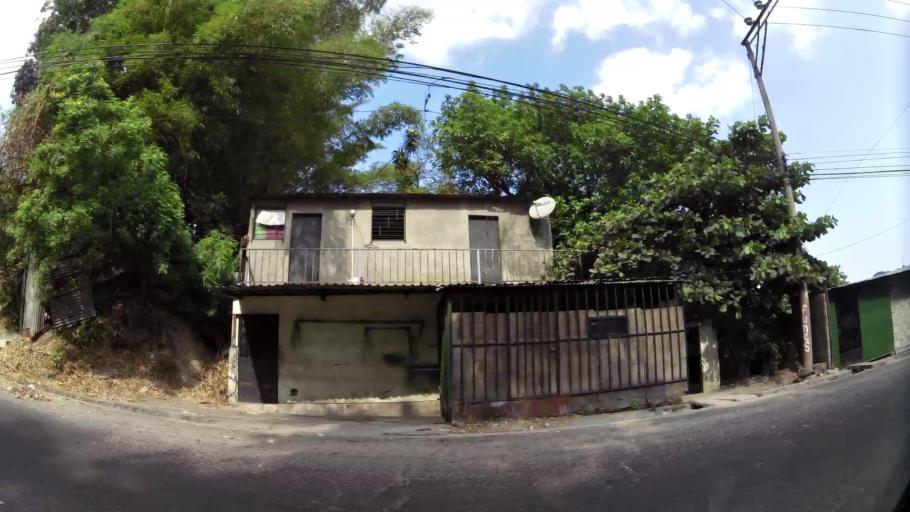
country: SV
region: San Salvador
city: Delgado
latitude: 13.7196
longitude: -89.1629
